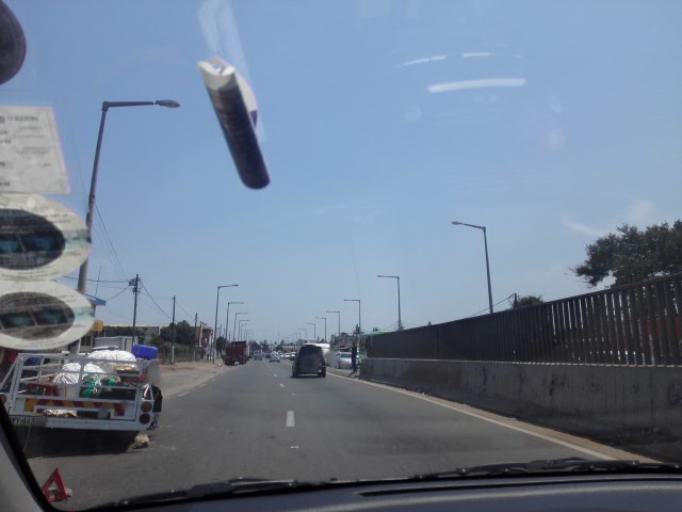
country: MZ
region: Maputo City
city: Maputo
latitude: -25.9089
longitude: 32.5659
